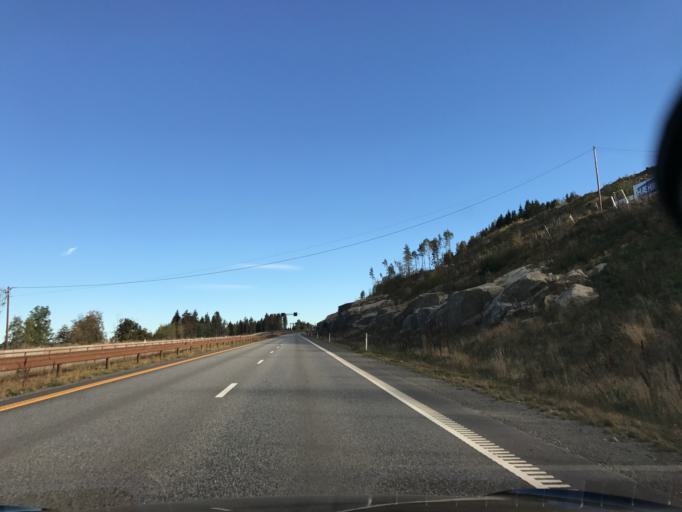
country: NO
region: Hedmark
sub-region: Stange
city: Stange
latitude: 60.5682
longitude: 11.2603
